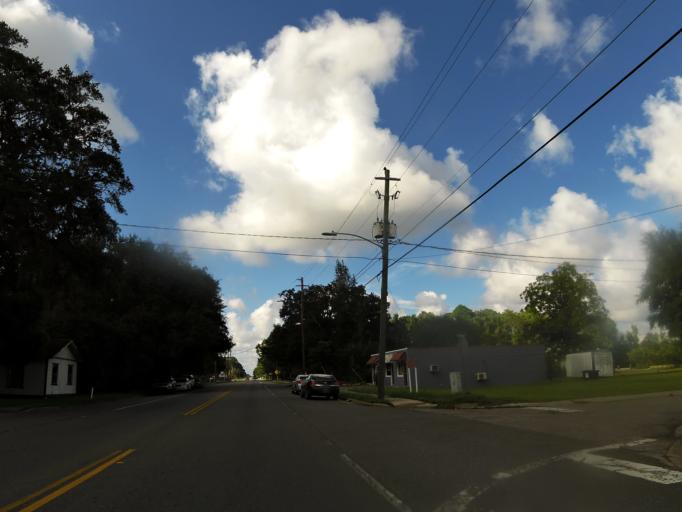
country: US
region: Georgia
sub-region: Camden County
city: Kingsland
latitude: 30.8055
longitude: -81.6913
